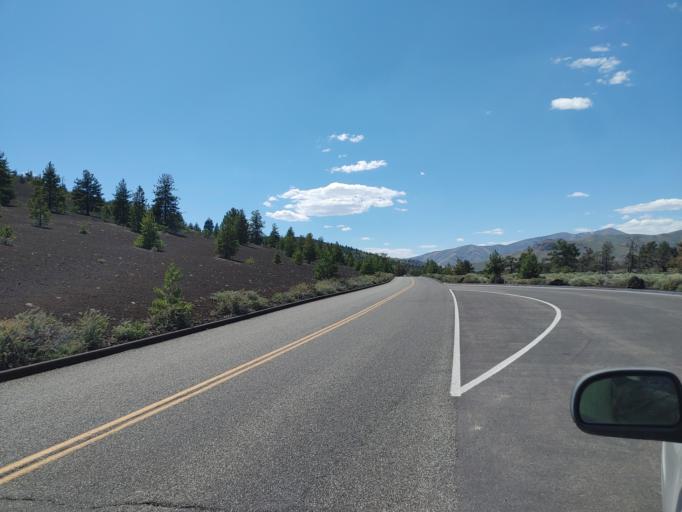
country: US
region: Idaho
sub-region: Butte County
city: Arco
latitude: 43.4537
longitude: -113.5460
